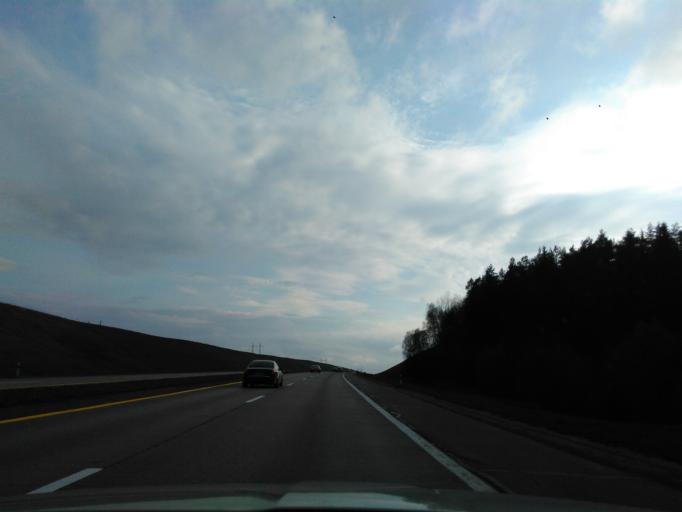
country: BY
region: Minsk
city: Astrashytski Haradok
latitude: 54.1036
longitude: 27.7964
